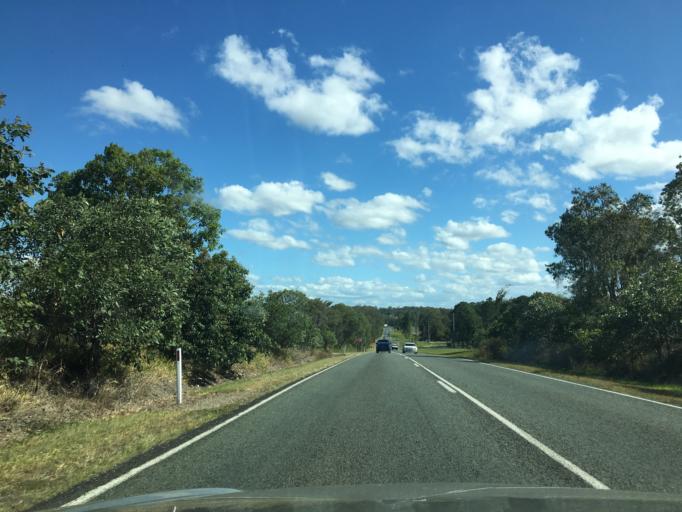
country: AU
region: Queensland
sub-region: Logan
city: Logan Reserve
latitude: -27.7421
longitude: 153.1271
